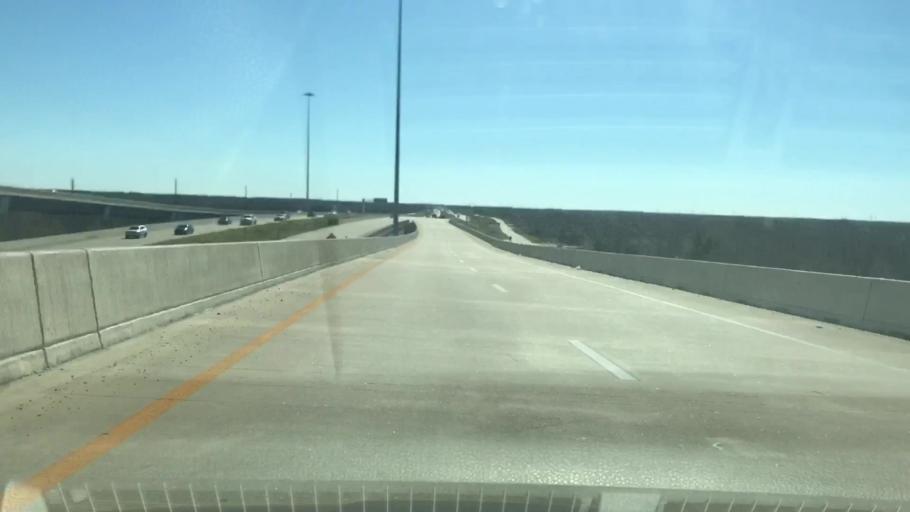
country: US
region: Texas
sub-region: Harris County
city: Cypress
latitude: 29.9950
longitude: -95.7692
